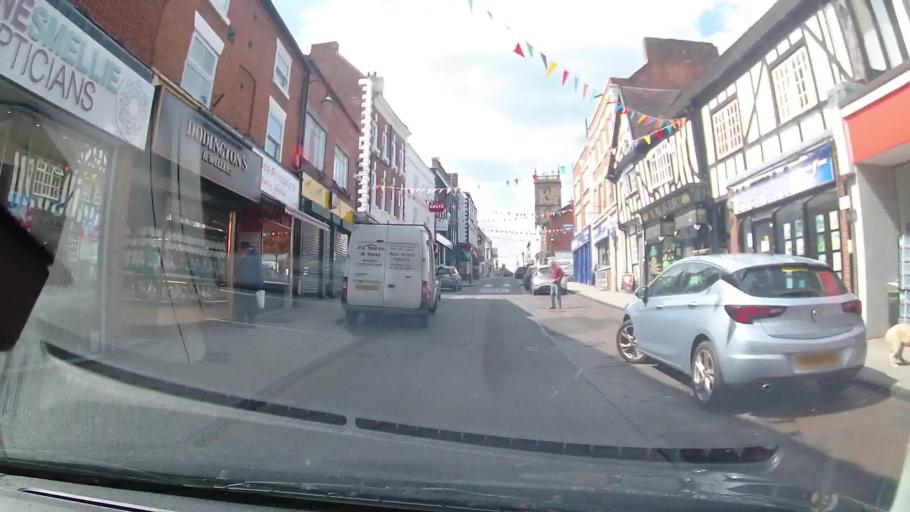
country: GB
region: England
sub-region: Shropshire
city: Whitchurch
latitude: 52.9688
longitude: -2.6844
